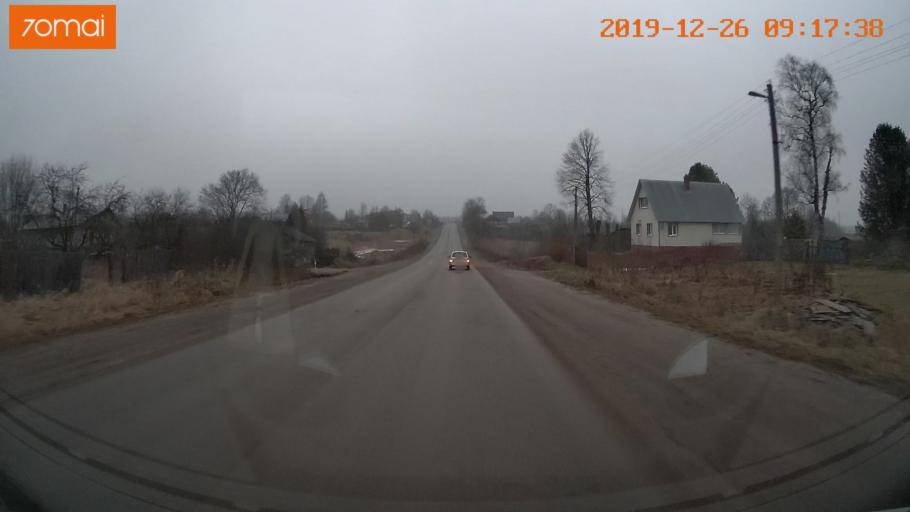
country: RU
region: Vologda
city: Gryazovets
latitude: 58.9315
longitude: 40.2406
